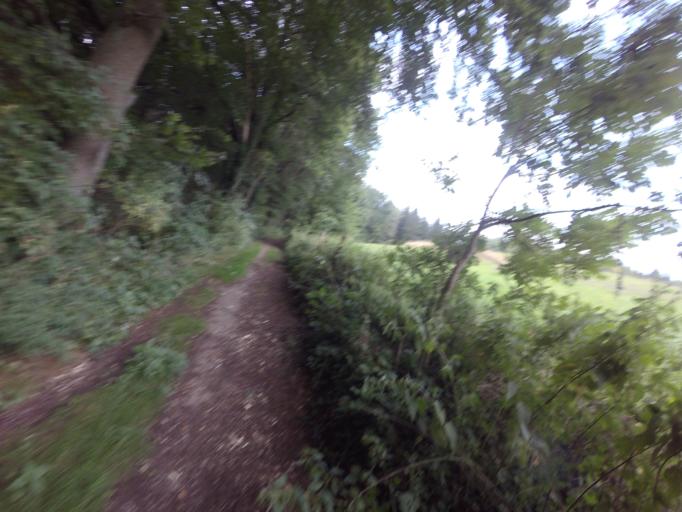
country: NL
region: Limburg
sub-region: Gemeente Vaals
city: Vaals
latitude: 50.7836
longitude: 6.0197
